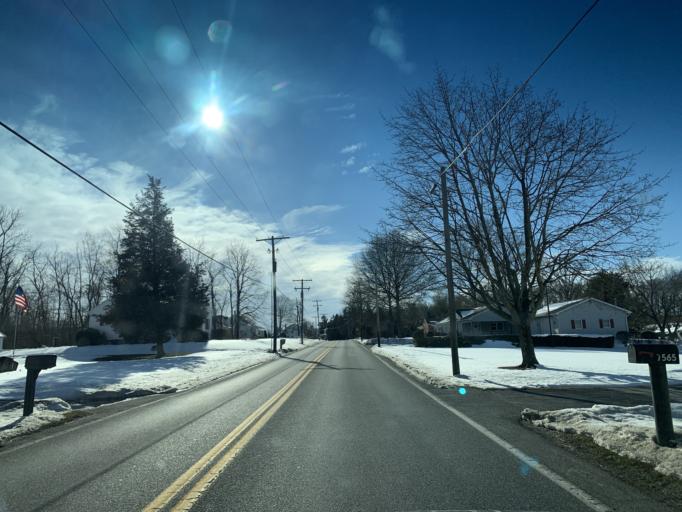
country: US
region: Pennsylvania
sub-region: York County
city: Dover
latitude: 40.0625
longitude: -76.9209
